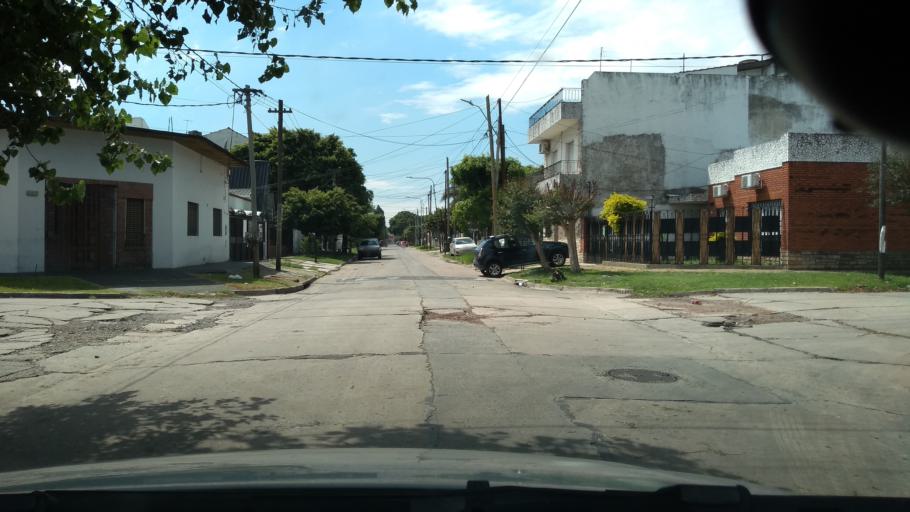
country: AR
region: Buenos Aires
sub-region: Partido de Moron
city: Moron
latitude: -34.6660
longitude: -58.6057
